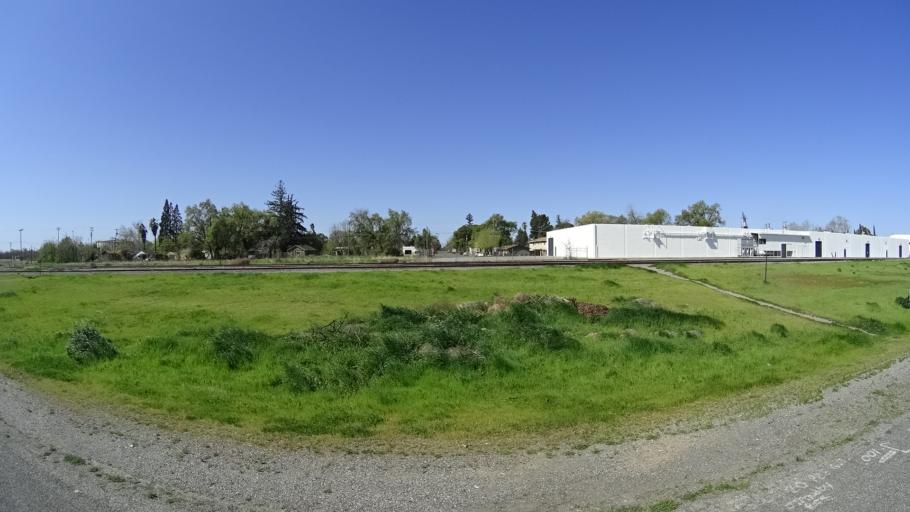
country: US
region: California
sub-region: Glenn County
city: Hamilton City
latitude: 39.7408
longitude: -122.0090
